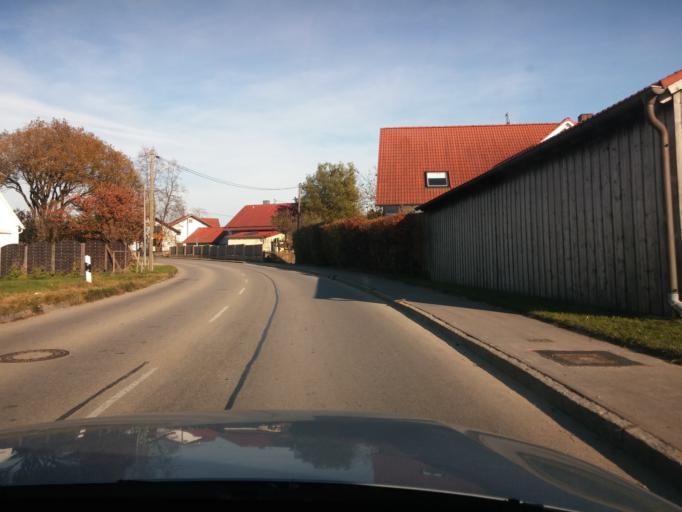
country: DE
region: Bavaria
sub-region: Upper Bavaria
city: Buch am Buchrain
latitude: 48.2153
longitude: 12.0000
